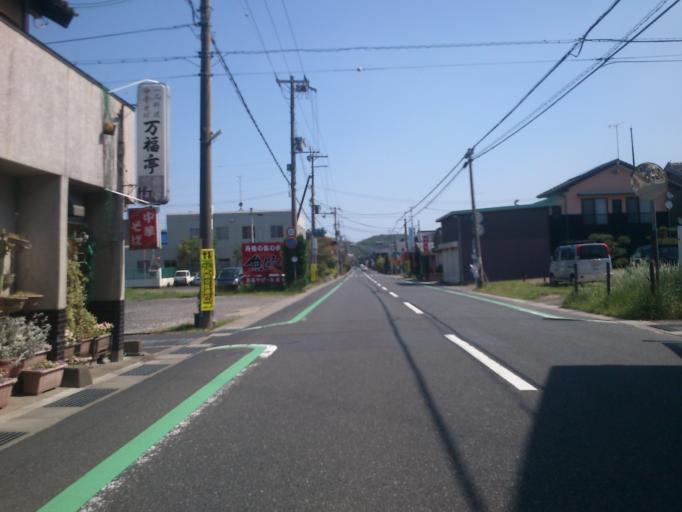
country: JP
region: Kyoto
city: Miyazu
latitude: 35.6850
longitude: 135.0316
